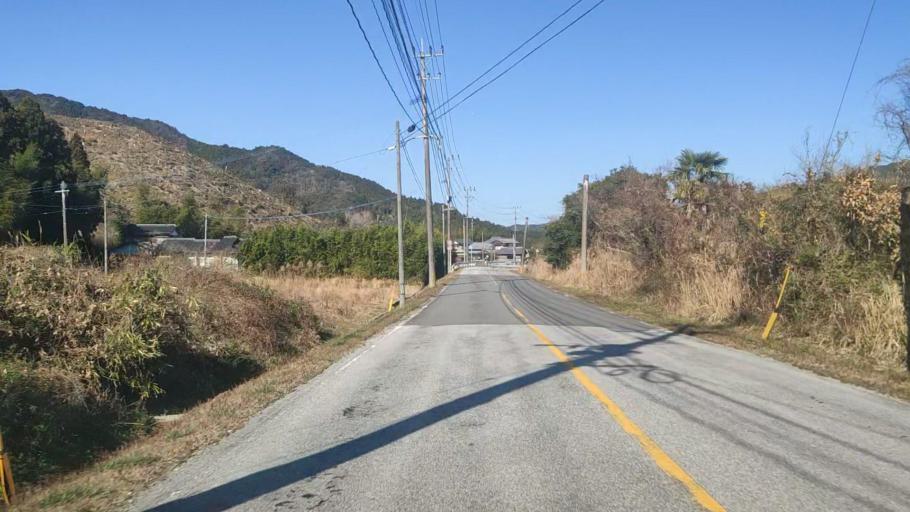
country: JP
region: Oita
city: Saiki
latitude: 32.9128
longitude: 131.9291
